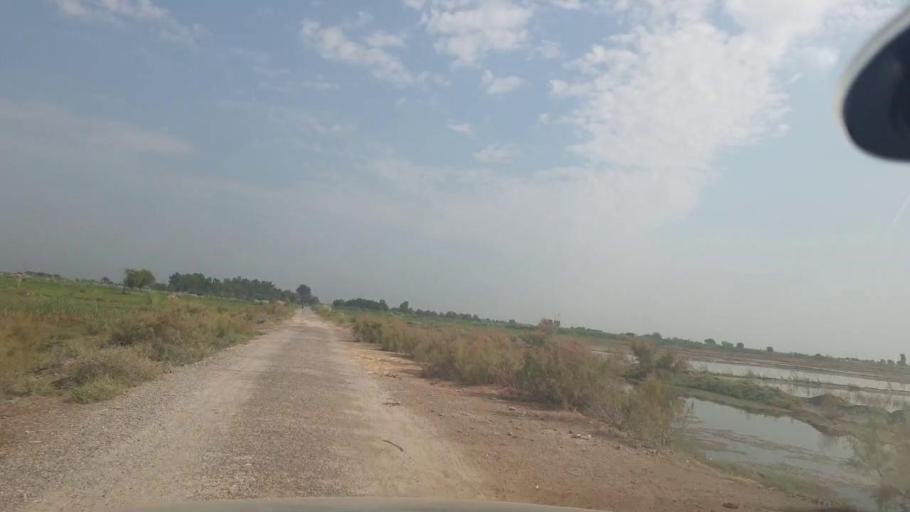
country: PK
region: Balochistan
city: Mehrabpur
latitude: 28.0479
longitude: 68.1225
